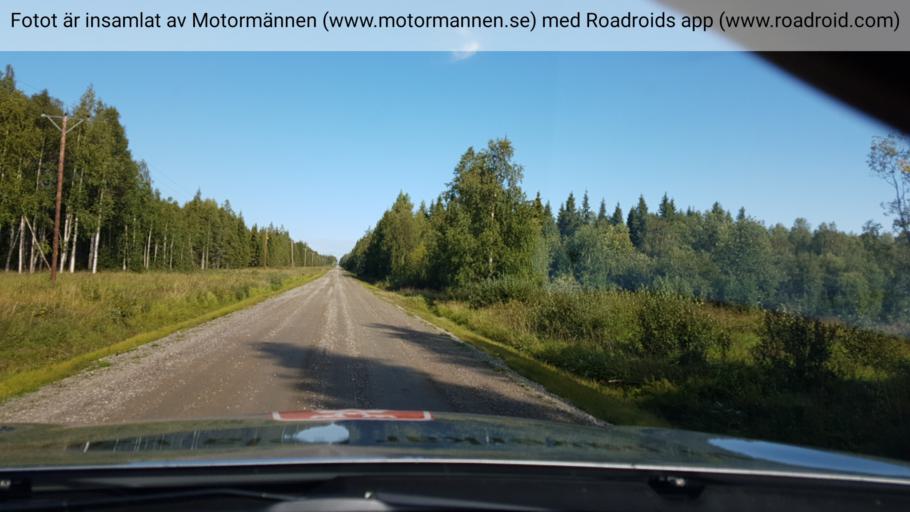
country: SE
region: Norrbotten
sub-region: Kalix Kommun
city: Kalix
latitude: 66.1677
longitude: 23.2169
